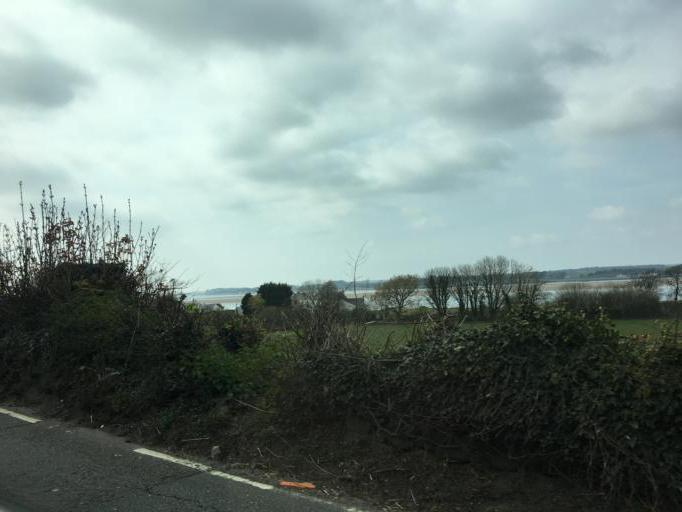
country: GB
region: Wales
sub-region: Gwynedd
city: Caernarfon
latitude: 53.1536
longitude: -4.2602
